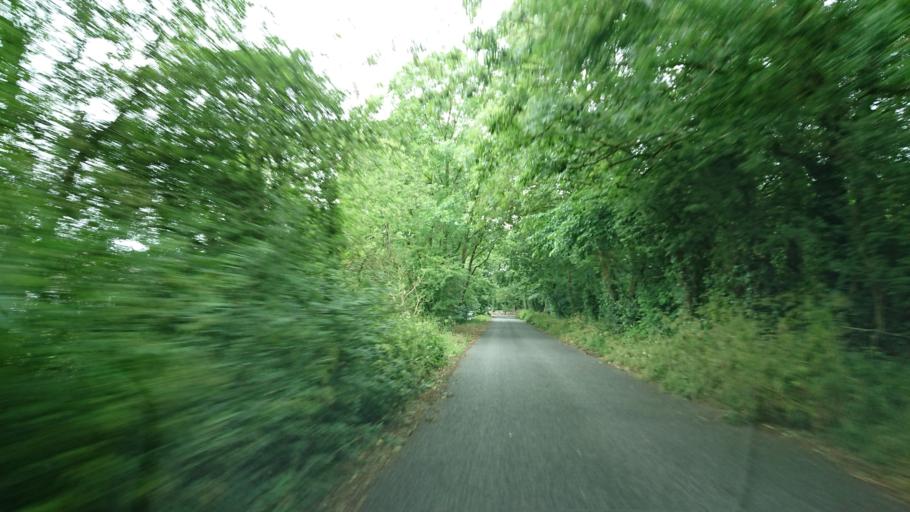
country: IE
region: Munster
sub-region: Waterford
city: Waterford
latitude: 52.2271
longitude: -7.1467
